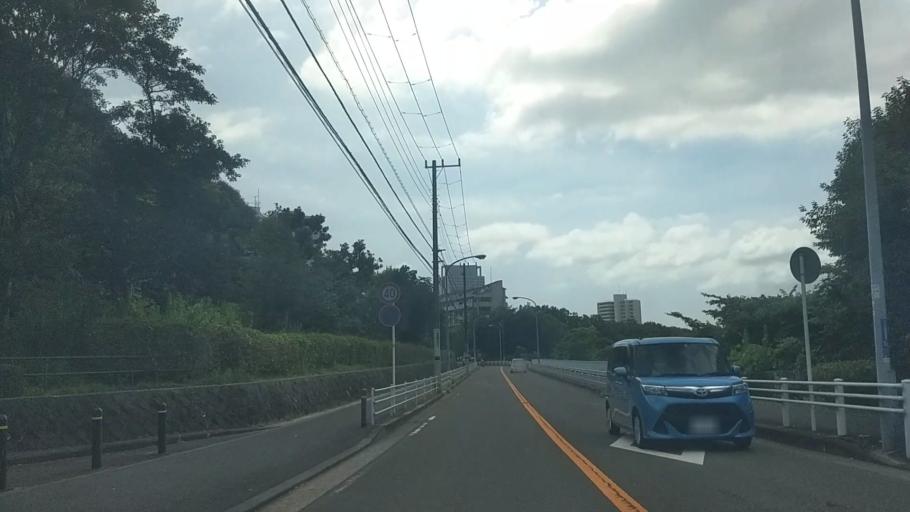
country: JP
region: Kanagawa
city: Yokosuka
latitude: 35.3574
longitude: 139.6370
